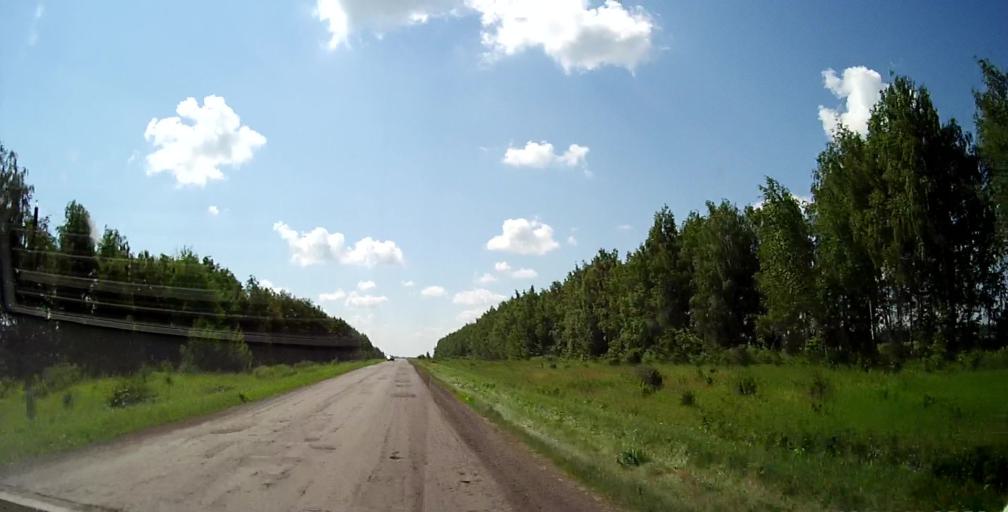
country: RU
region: Lipetsk
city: Chaplygin
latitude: 53.3646
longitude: 39.9183
